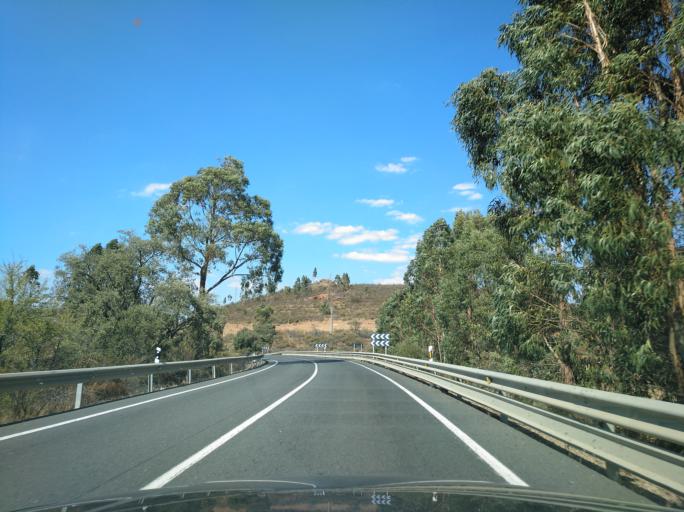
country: ES
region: Andalusia
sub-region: Provincia de Huelva
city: Alosno
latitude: 37.5773
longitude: -7.1132
